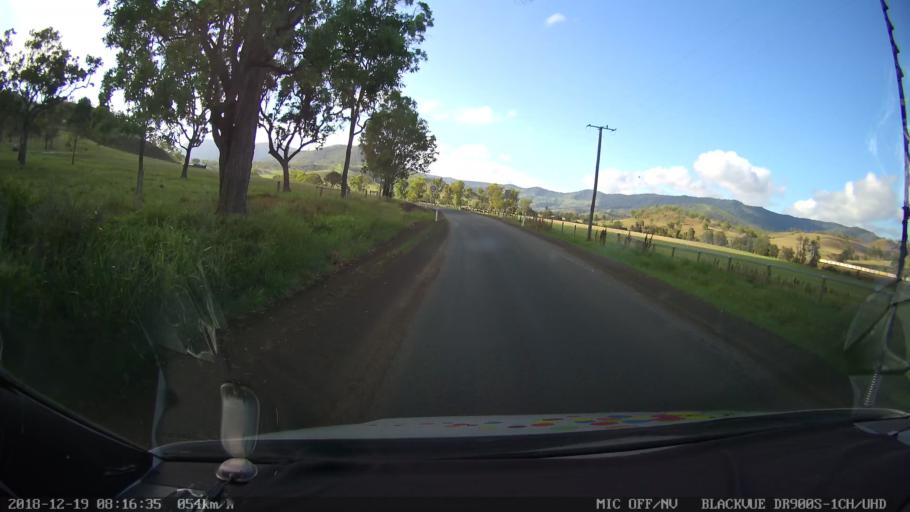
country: AU
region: New South Wales
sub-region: Kyogle
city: Kyogle
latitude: -28.2590
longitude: 152.9066
